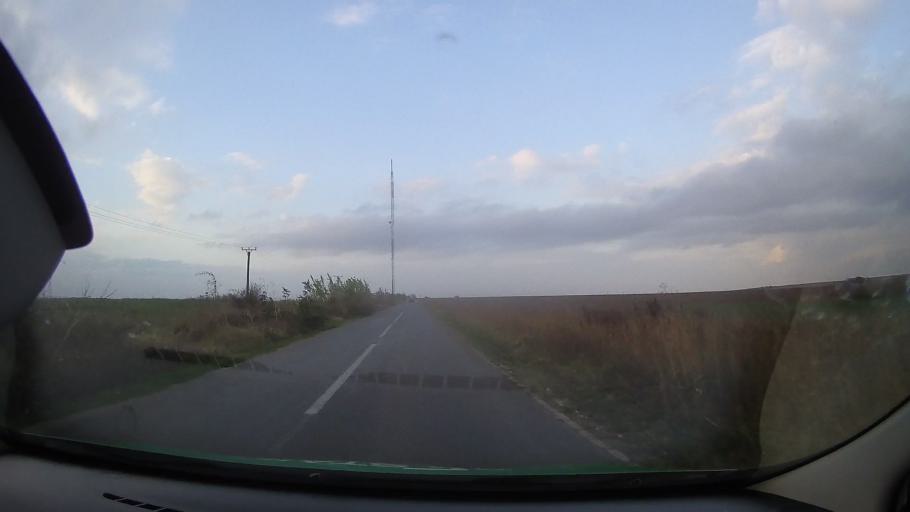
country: RO
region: Constanta
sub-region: Comuna Dobromir
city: Dobromir
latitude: 44.0450
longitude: 27.7545
